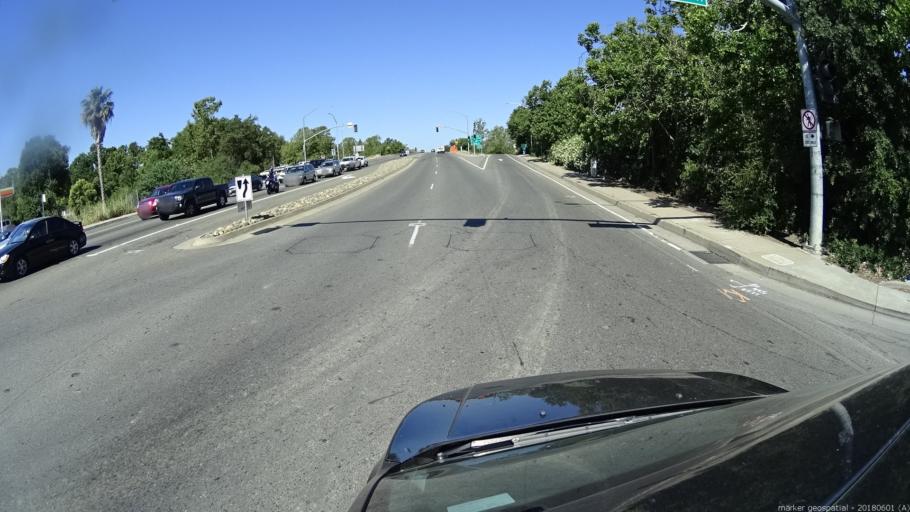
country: US
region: California
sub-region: Sacramento County
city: Parkway
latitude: 38.4813
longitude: -121.5076
